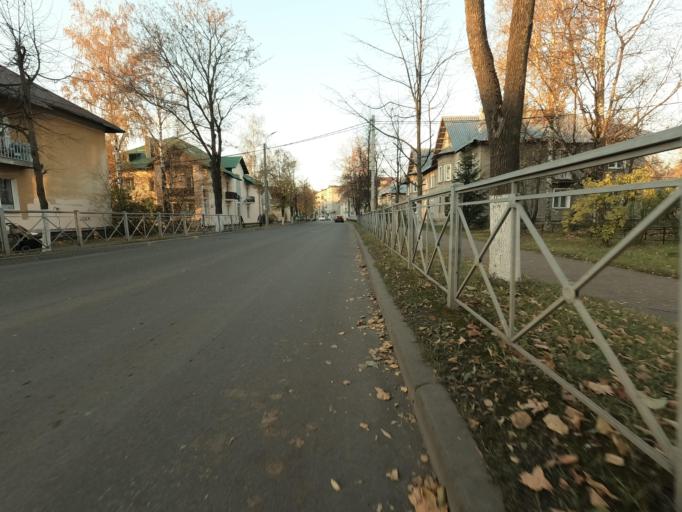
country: RU
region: Leningrad
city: Kirovsk
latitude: 59.8750
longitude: 30.9912
